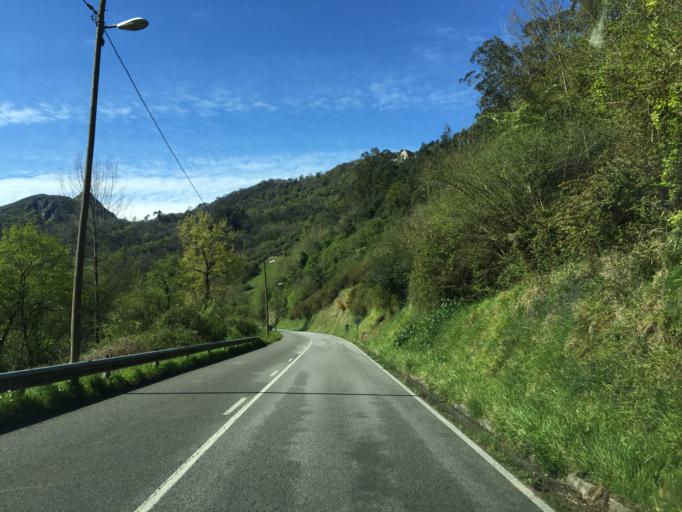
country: ES
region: Asturias
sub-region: Province of Asturias
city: Proaza
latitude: 43.3267
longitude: -5.9904
